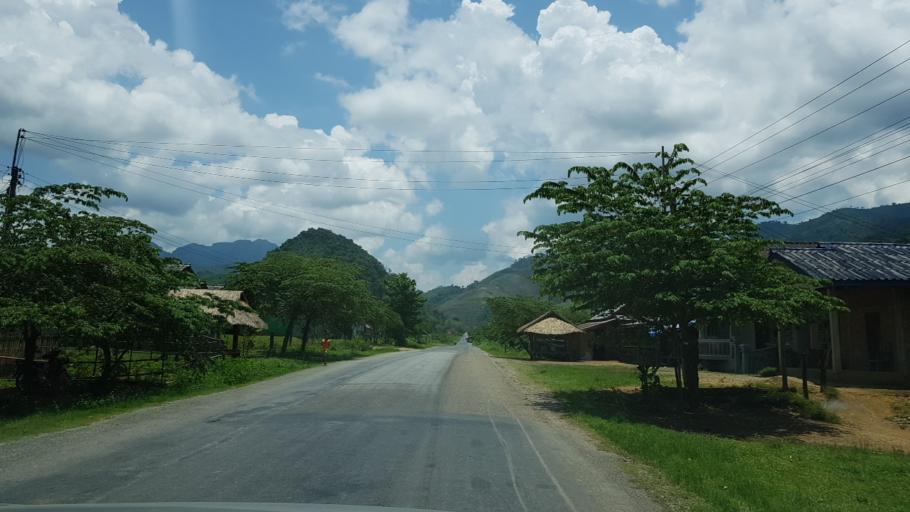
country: LA
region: Vientiane
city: Muang Kasi
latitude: 19.1291
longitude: 102.2678
